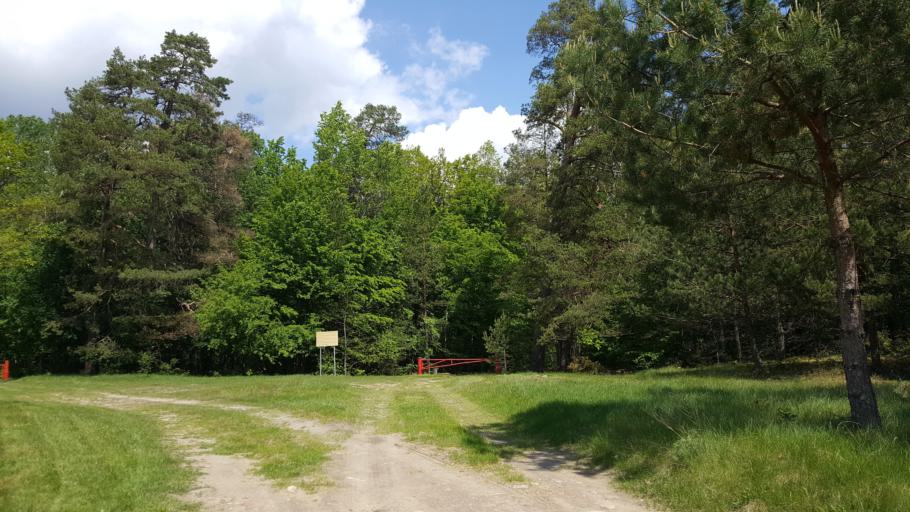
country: BY
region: Brest
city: Kamyanyuki
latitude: 52.4957
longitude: 23.9621
